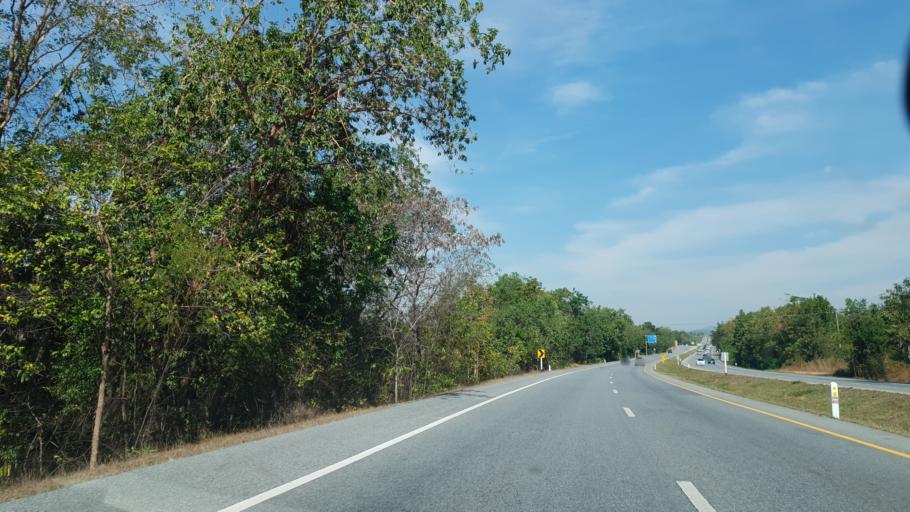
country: TH
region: Uttaradit
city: Thong Saen Khan
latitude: 17.4276
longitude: 100.2261
